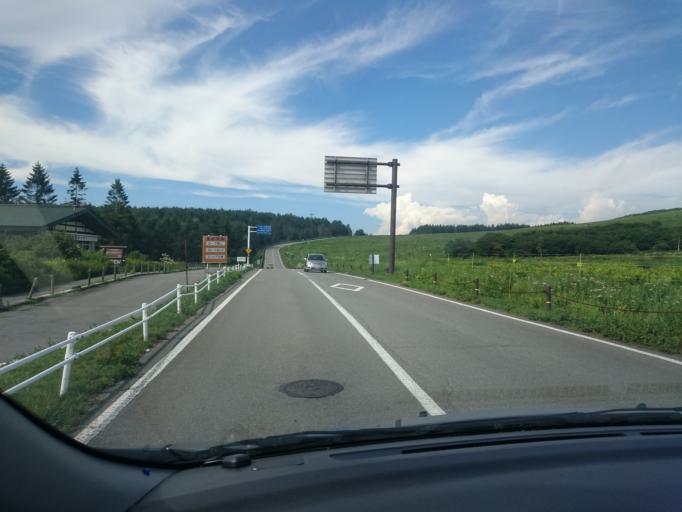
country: JP
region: Nagano
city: Suwa
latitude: 36.0978
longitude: 138.1687
